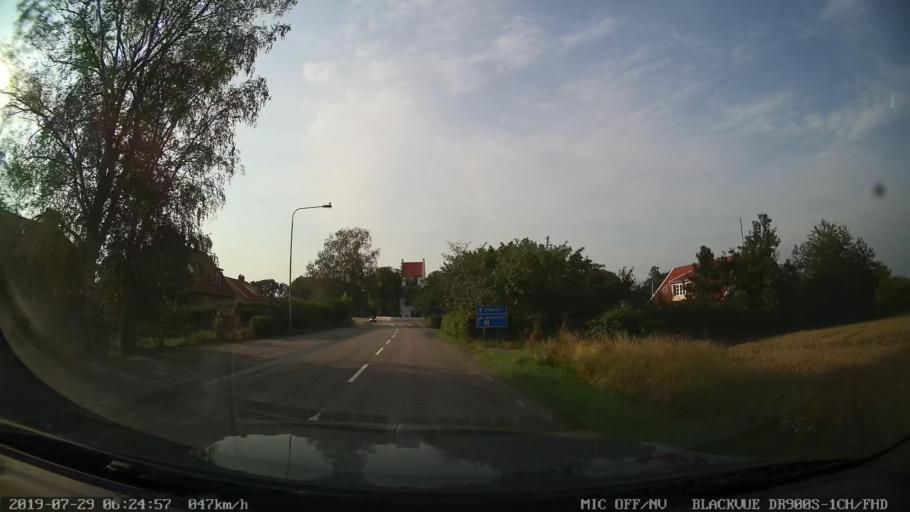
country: SE
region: Skane
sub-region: Helsingborg
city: Odakra
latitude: 56.1075
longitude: 12.6925
